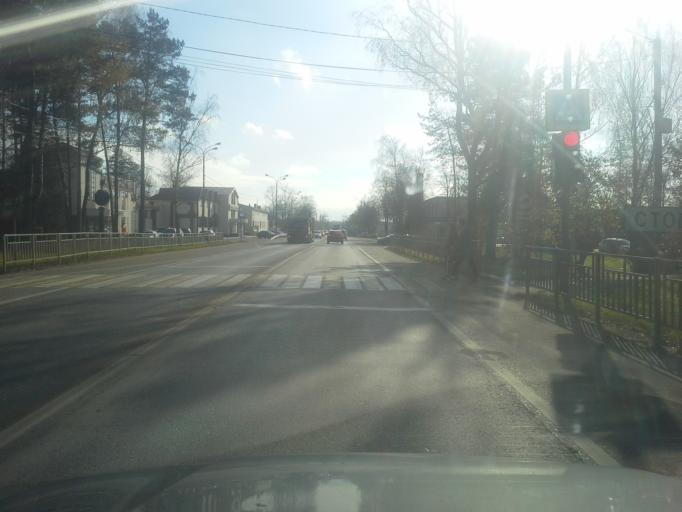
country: RU
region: Moskovskaya
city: Bol'shiye Vyazemy
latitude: 55.6453
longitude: 36.9762
